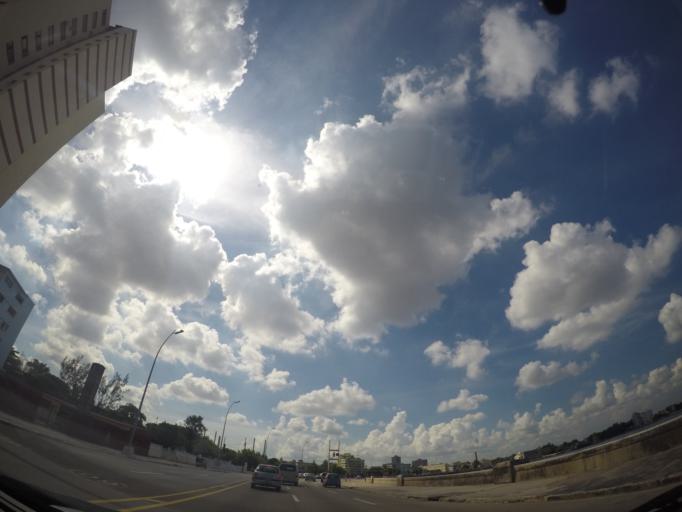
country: CU
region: La Habana
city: Havana
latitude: 23.1356
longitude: -82.4082
